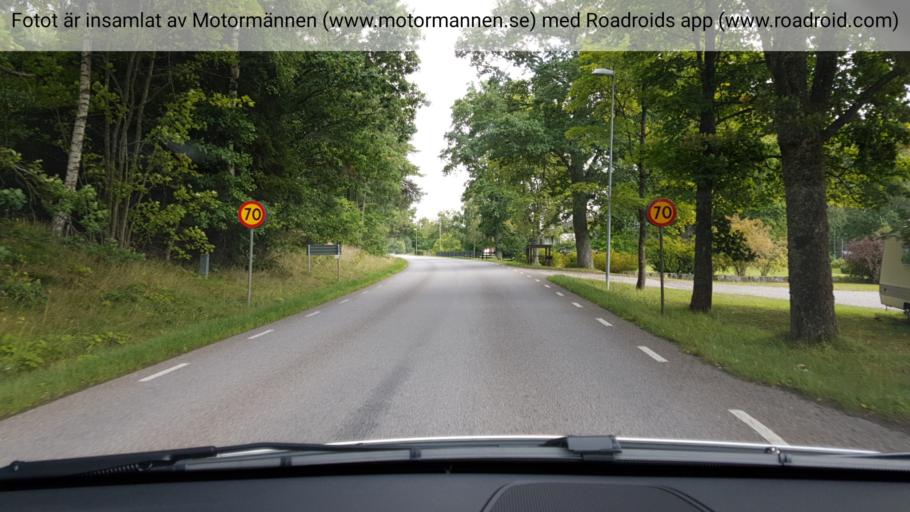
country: SE
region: Vaestra Goetaland
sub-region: Essunga Kommun
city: Nossebro
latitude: 58.1861
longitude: 12.7949
